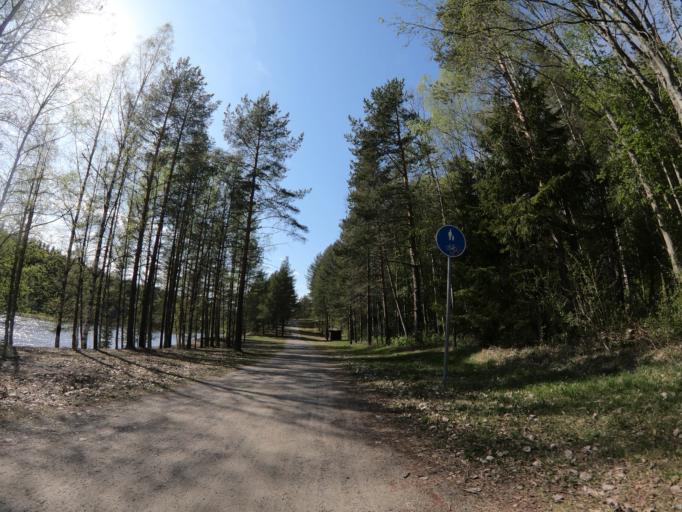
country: SE
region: Vaesterbotten
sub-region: Umea Kommun
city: Roback
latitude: 63.8296
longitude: 20.1684
